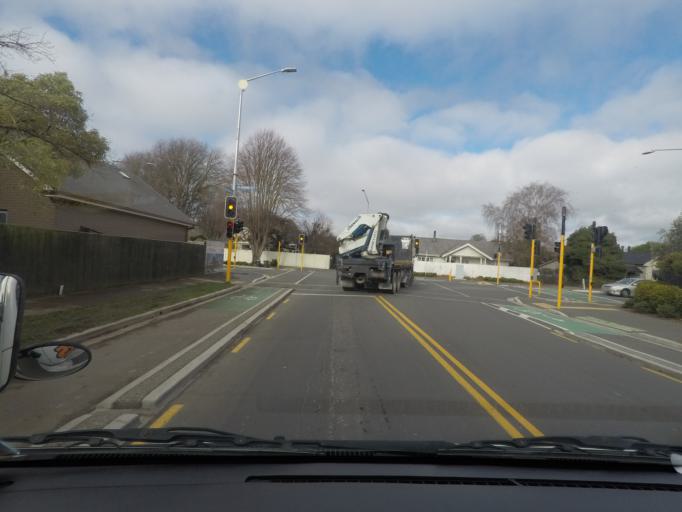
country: NZ
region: Canterbury
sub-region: Christchurch City
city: Christchurch
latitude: -43.5087
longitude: 172.6309
